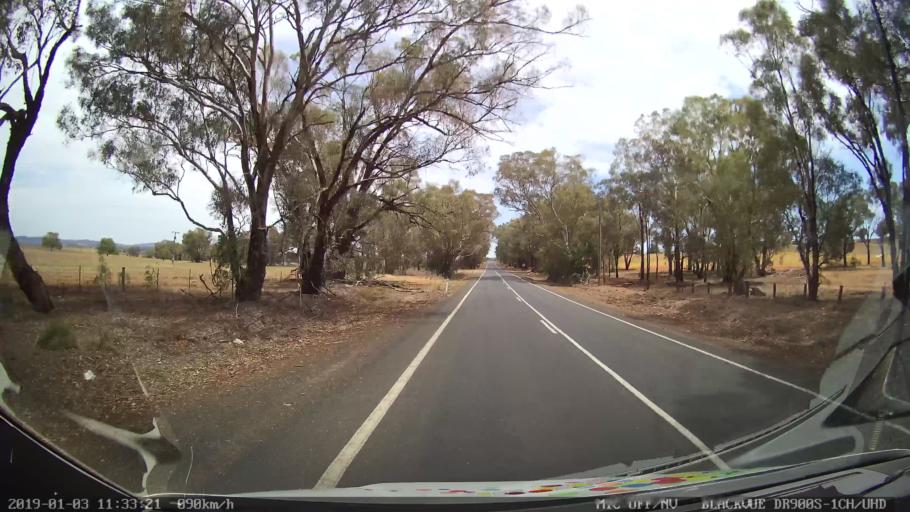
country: AU
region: New South Wales
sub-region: Weddin
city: Grenfell
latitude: -33.9478
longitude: 148.1714
